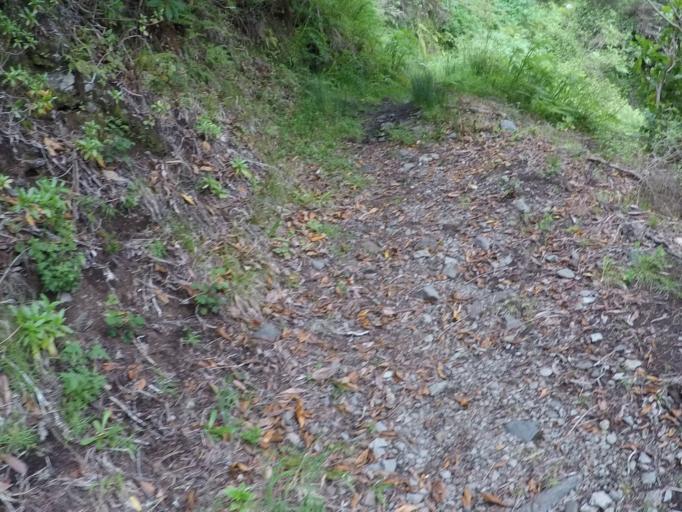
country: PT
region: Madeira
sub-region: Camara de Lobos
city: Curral das Freiras
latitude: 32.7356
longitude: -16.9927
